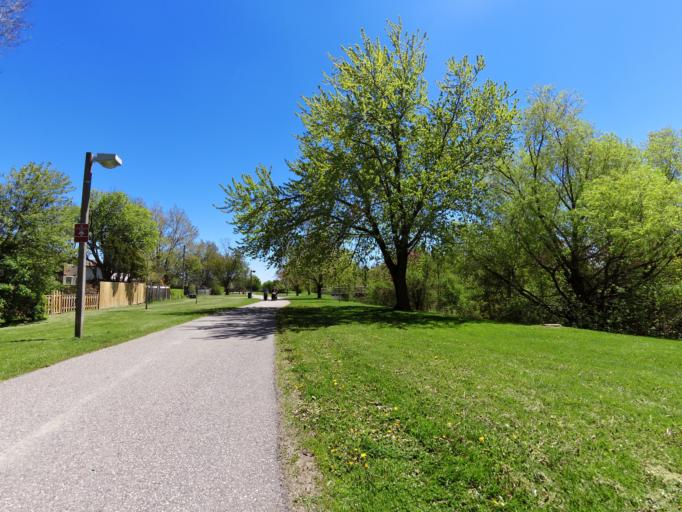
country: CA
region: Ontario
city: Brampton
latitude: 43.7151
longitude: -79.7108
